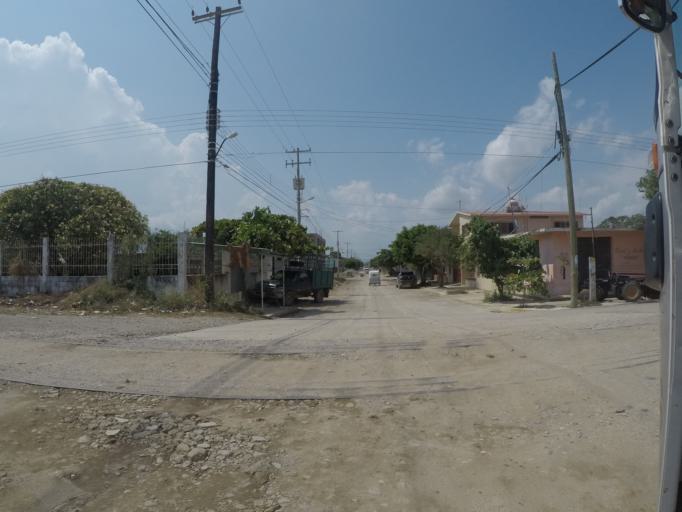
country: MX
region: Oaxaca
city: Union Hidalgo
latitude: 16.4692
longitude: -94.8303
